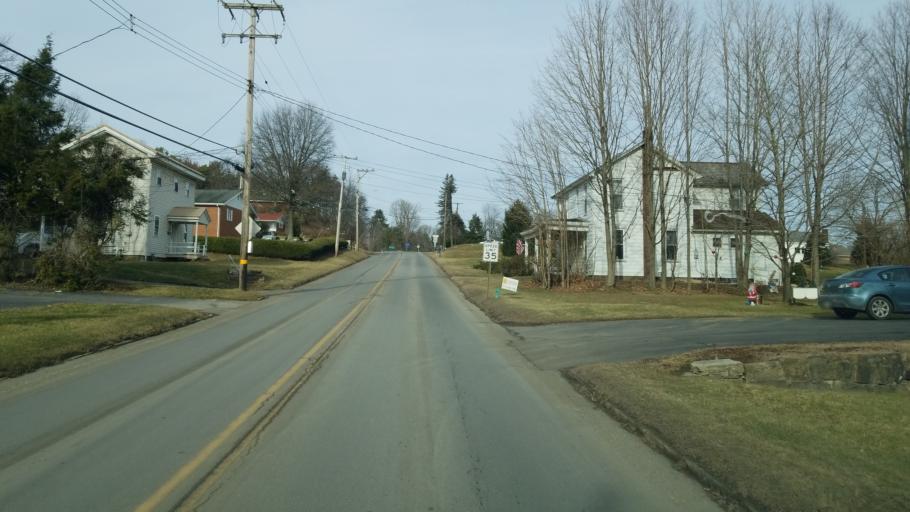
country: US
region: Pennsylvania
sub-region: Jefferson County
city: Punxsutawney
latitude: 40.9510
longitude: -78.9974
